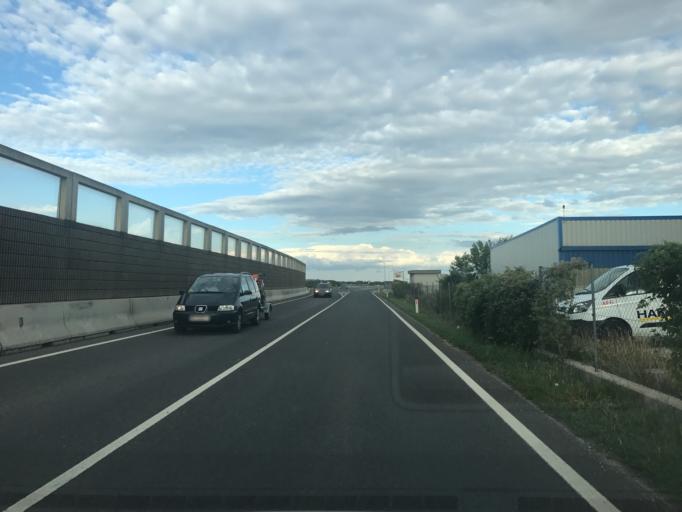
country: AT
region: Lower Austria
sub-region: Politischer Bezirk Wiener Neustadt
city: Theresienfeld
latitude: 47.8463
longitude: 16.2491
